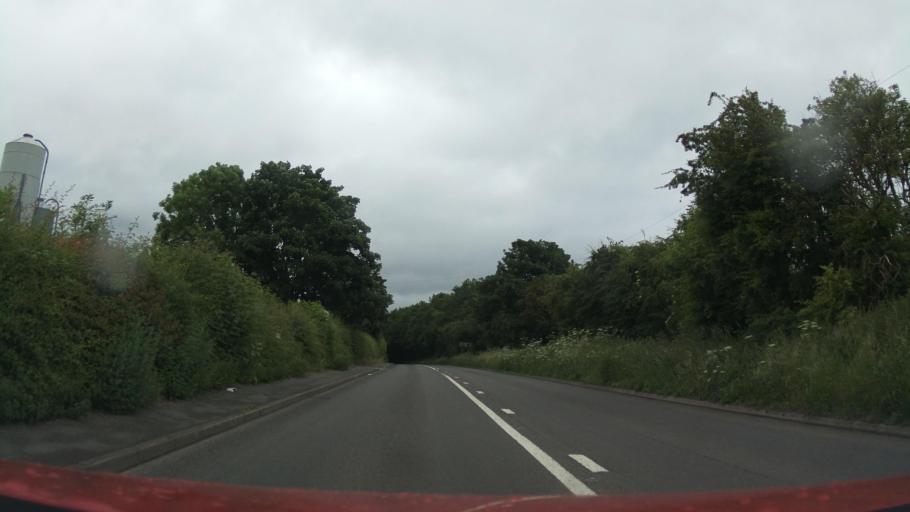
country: GB
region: England
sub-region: Staffordshire
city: Burton upon Trent
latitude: 52.8448
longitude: -1.6754
